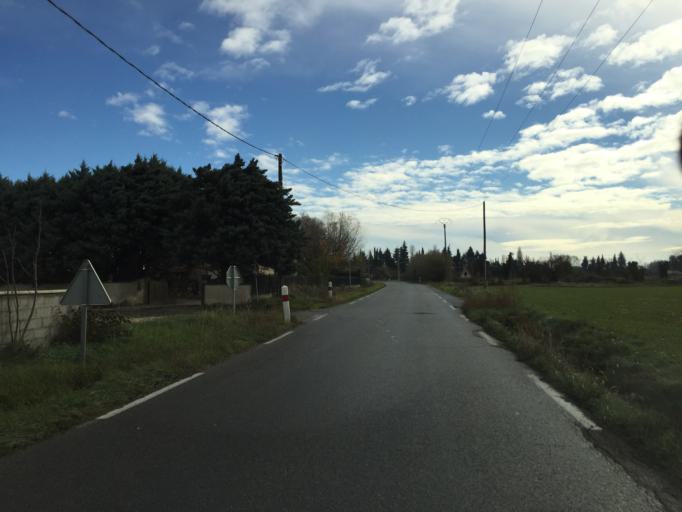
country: FR
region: Provence-Alpes-Cote d'Azur
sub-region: Departement du Vaucluse
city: Althen-des-Paluds
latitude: 43.9764
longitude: 4.9740
